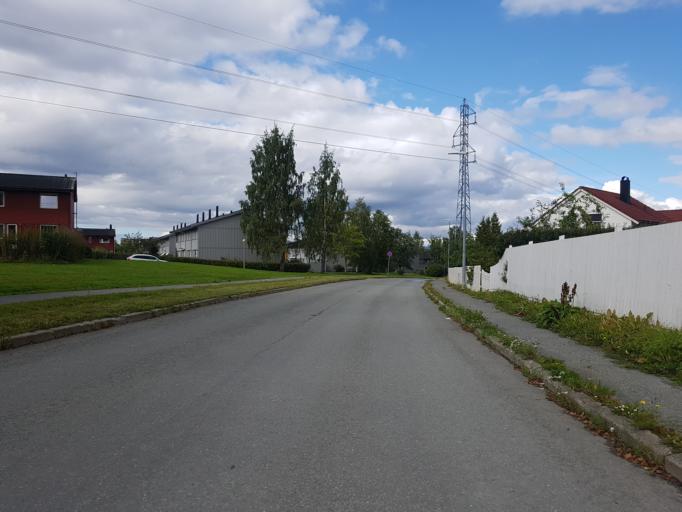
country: NO
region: Sor-Trondelag
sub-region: Trondheim
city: Trondheim
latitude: 63.4269
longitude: 10.4539
